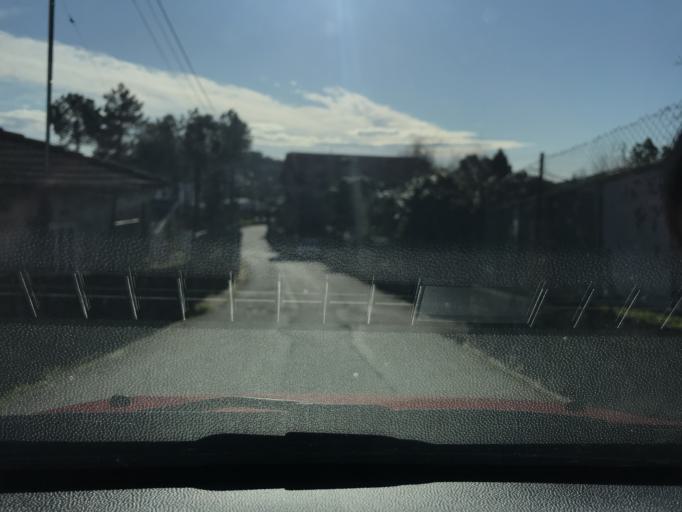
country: PT
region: Braga
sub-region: Vila Nova de Famalicao
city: Vila Nova de Famalicao
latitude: 41.4182
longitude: -8.5047
